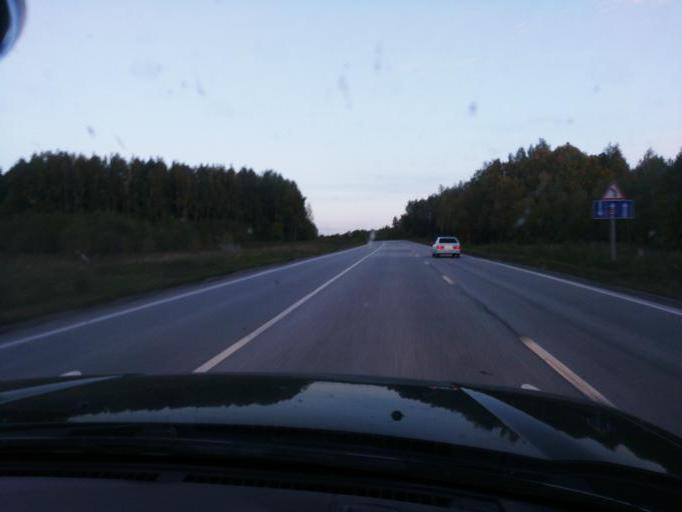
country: RU
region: Perm
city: Verkhnechusovskiye Gorodki
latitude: 58.2877
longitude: 56.8974
